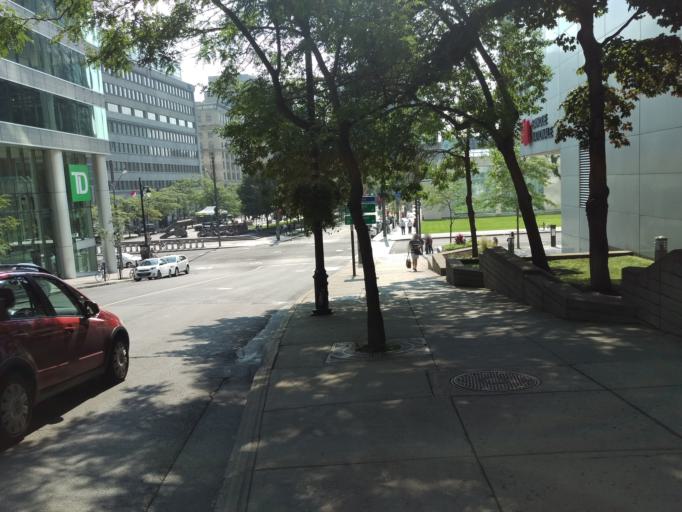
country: CA
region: Quebec
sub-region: Montreal
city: Montreal
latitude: 45.5024
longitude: -73.5640
